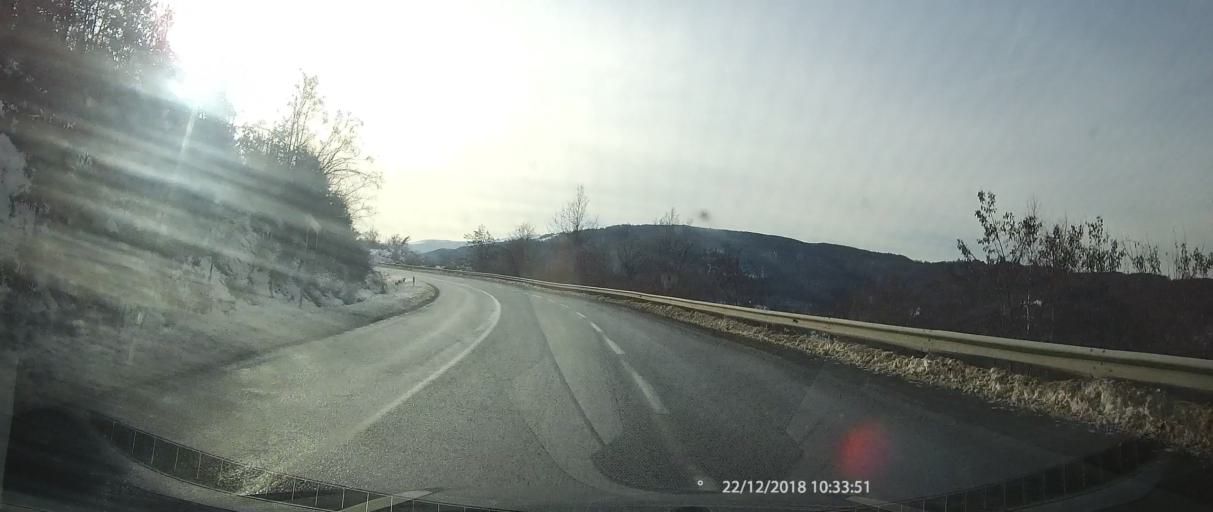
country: MK
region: Kriva Palanka
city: Kriva Palanka
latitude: 42.2190
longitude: 22.4445
